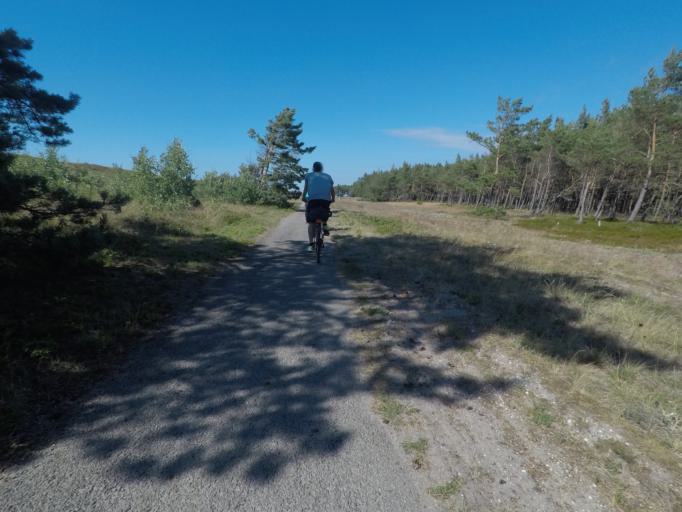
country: LT
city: Neringa
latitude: 55.5200
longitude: 21.0951
